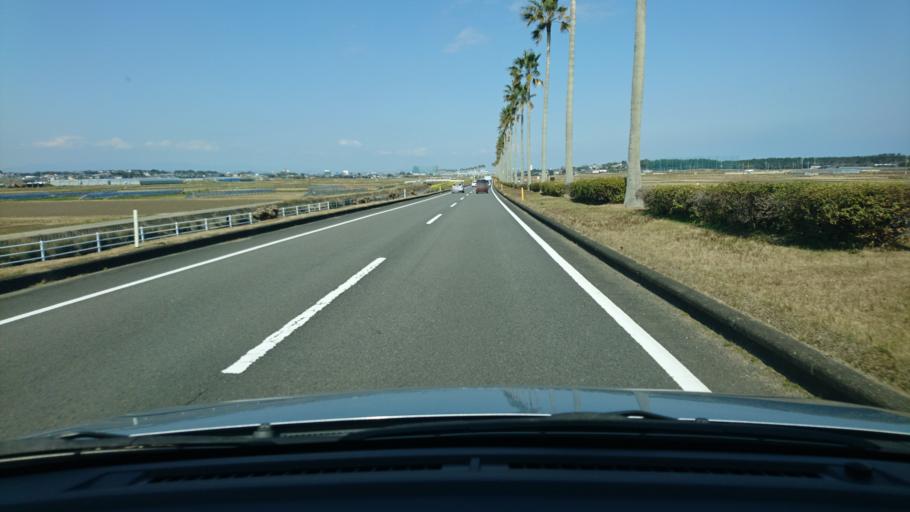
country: JP
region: Miyazaki
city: Miyazaki-shi
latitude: 31.8503
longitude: 131.4435
